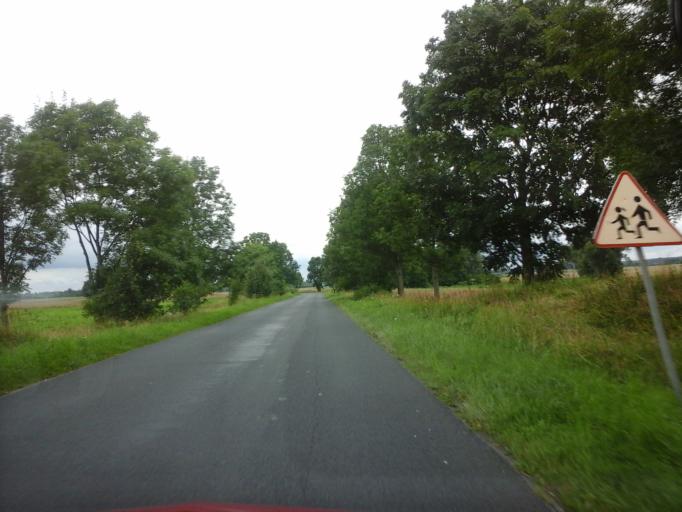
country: PL
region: West Pomeranian Voivodeship
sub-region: Powiat choszczenski
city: Bierzwnik
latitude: 53.0449
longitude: 15.6871
